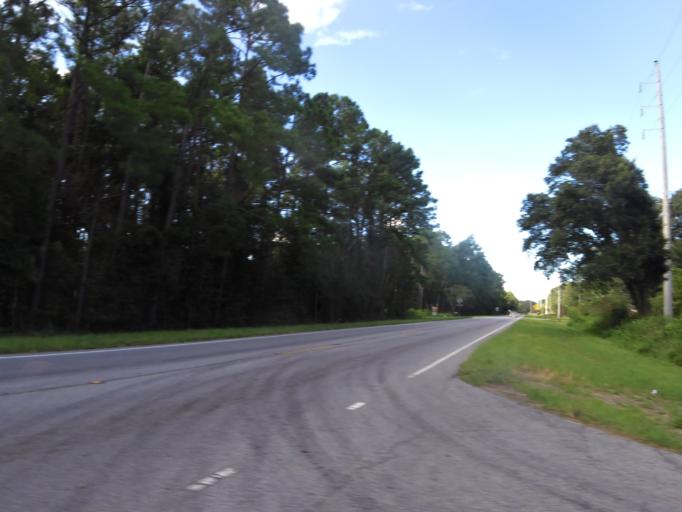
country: US
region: Georgia
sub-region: Glynn County
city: Country Club Estates
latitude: 31.2582
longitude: -81.4409
